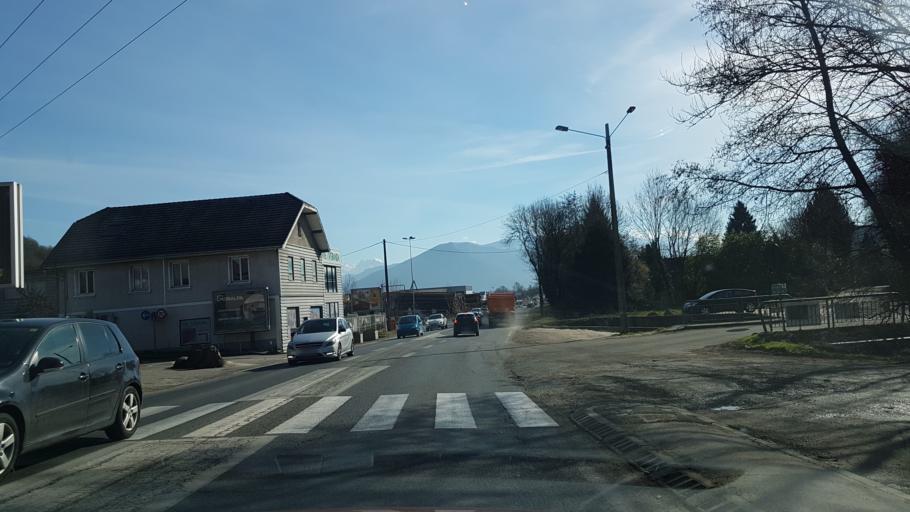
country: FR
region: Rhone-Alpes
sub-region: Departement de la Haute-Savoie
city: Poisy
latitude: 45.9431
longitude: 6.0596
